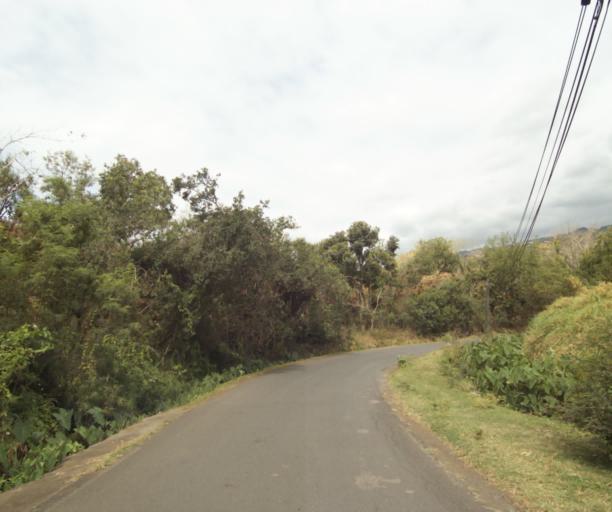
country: RE
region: Reunion
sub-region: Reunion
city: Saint-Paul
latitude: -20.9913
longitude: 55.3032
